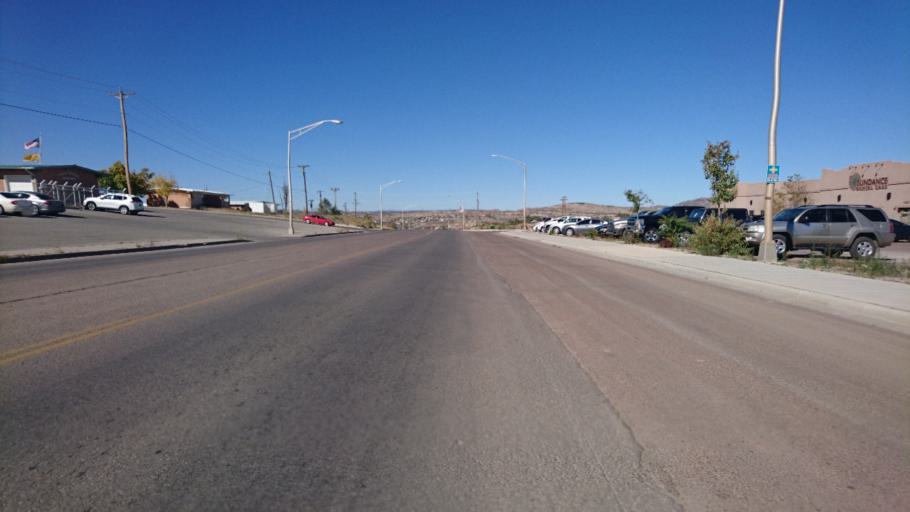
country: US
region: New Mexico
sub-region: McKinley County
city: Gallup
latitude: 35.5137
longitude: -108.7386
